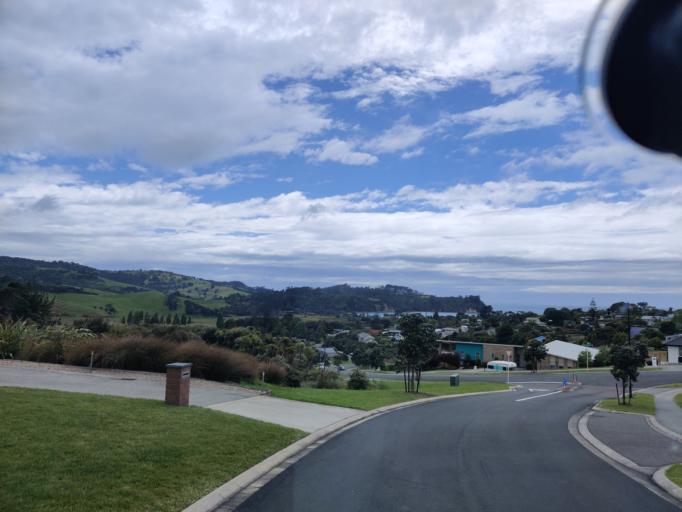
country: NZ
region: Auckland
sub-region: Auckland
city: Rothesay Bay
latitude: -36.5683
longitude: 174.6850
